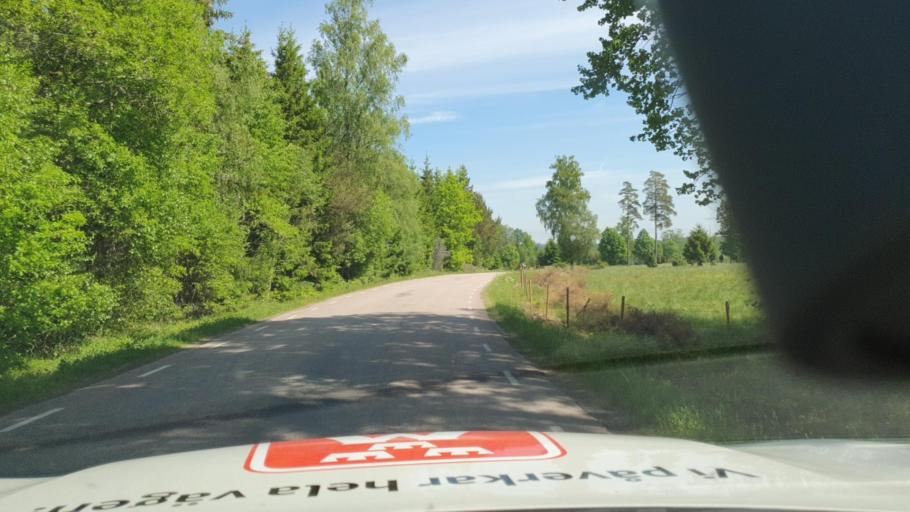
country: SE
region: Vaestra Goetaland
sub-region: Herrljunga Kommun
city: Herrljunga
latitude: 58.0189
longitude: 13.0948
